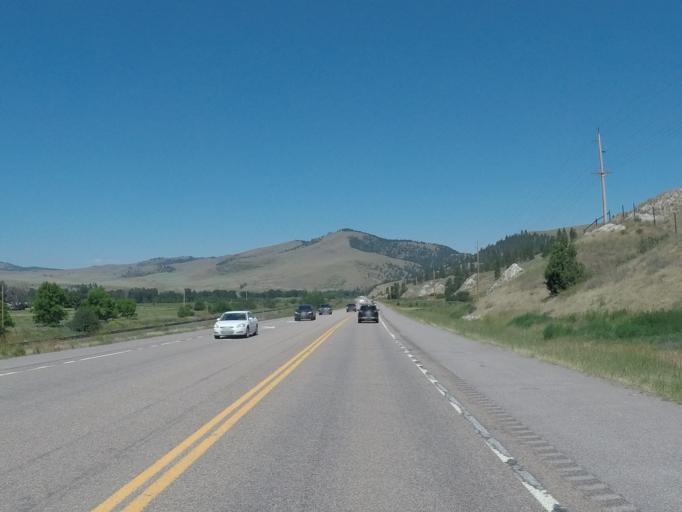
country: US
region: Montana
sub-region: Missoula County
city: Frenchtown
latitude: 47.2310
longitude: -114.1513
